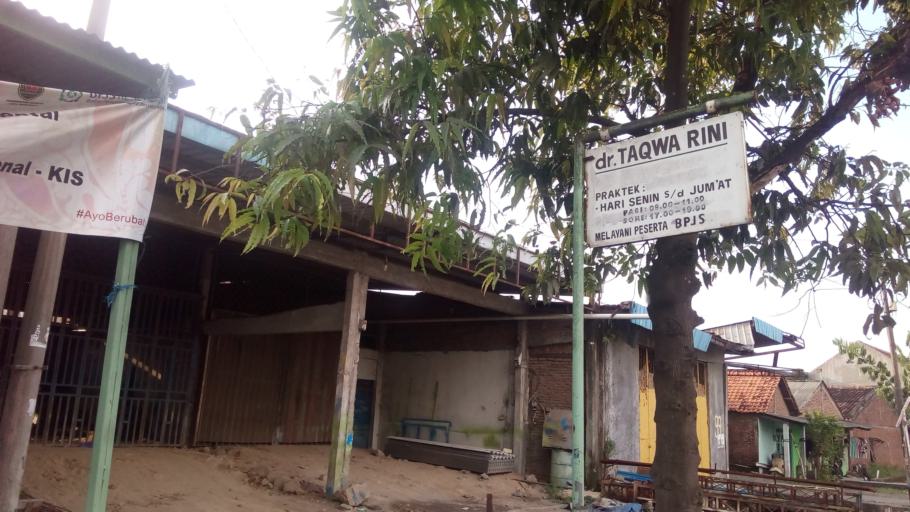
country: ID
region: Central Java
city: Semarang
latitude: -6.9605
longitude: 110.4788
